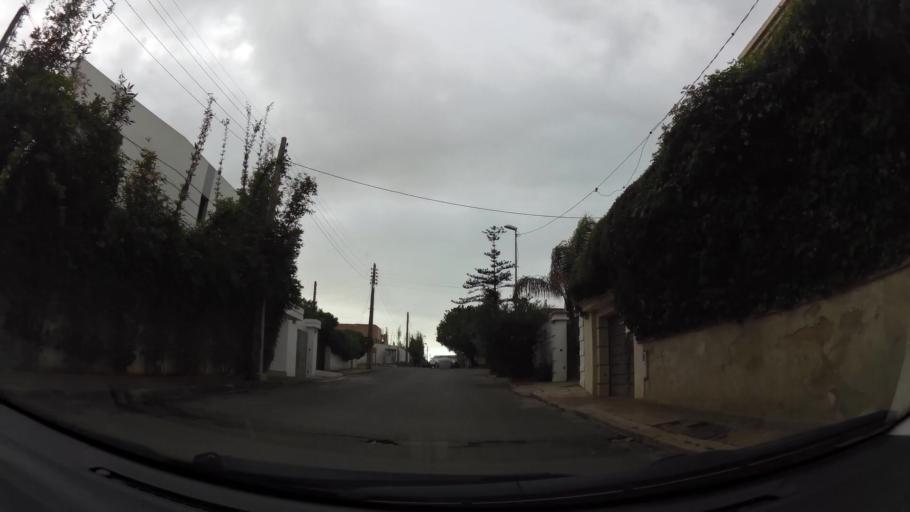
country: MA
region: Grand Casablanca
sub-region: Casablanca
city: Casablanca
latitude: 33.5764
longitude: -7.6780
